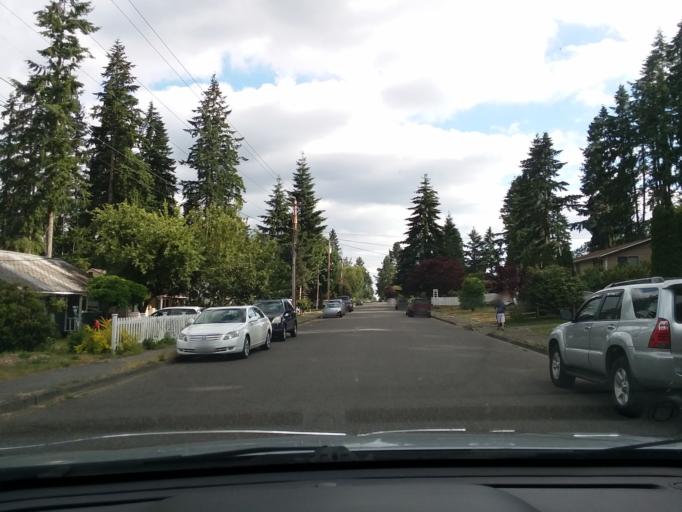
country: US
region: Washington
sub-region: Snohomish County
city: Mountlake Terrace
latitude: 47.7900
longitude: -122.3030
